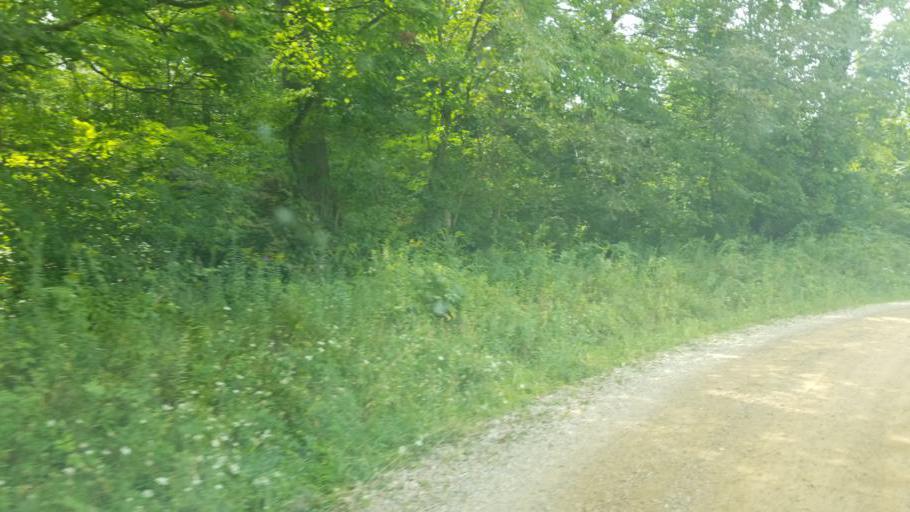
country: US
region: Ohio
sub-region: Knox County
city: Danville
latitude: 40.4784
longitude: -82.3068
